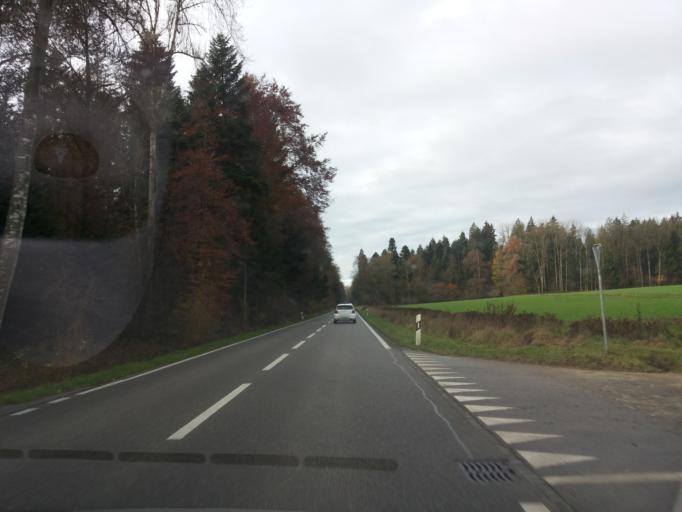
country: CH
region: Bern
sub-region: Oberaargau
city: Roggwil
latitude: 47.2270
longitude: 7.8240
